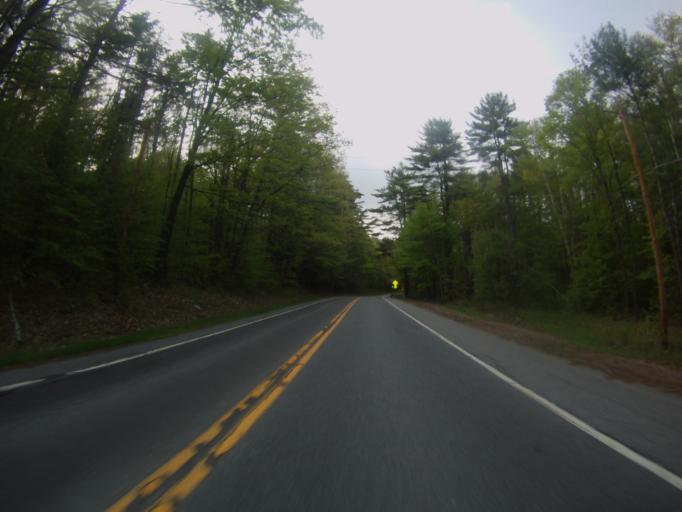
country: US
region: New York
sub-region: Essex County
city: Ticonderoga
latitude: 43.7866
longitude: -73.4878
